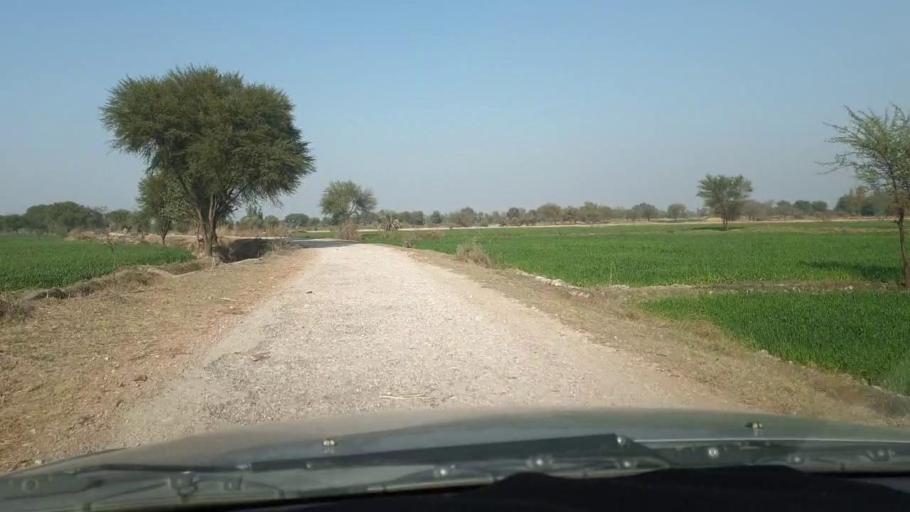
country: PK
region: Sindh
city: Mirpur Mathelo
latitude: 27.9306
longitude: 69.5632
